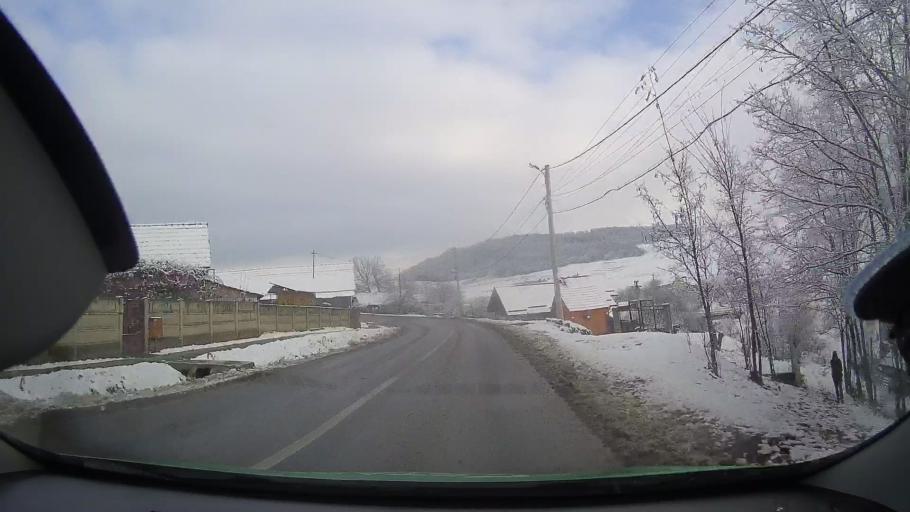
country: RO
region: Mures
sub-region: Comuna Atintis
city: Atintis
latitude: 46.4275
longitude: 24.1031
